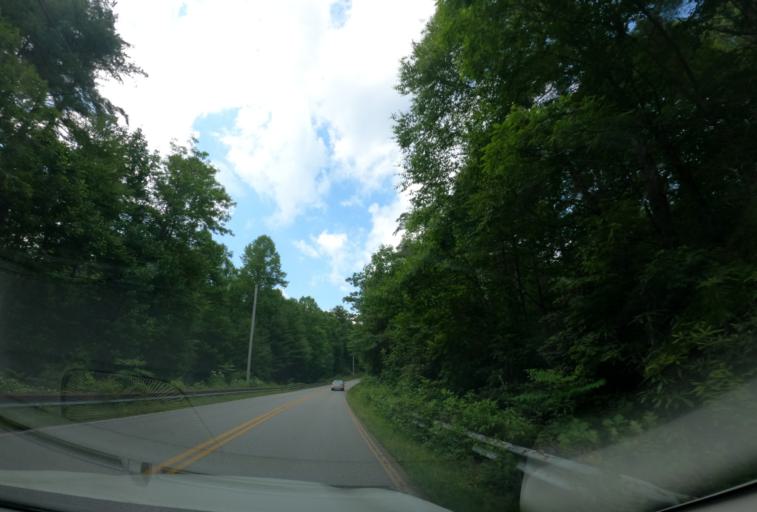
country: US
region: South Carolina
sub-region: Oconee County
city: Walhalla
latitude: 35.0514
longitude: -83.0127
